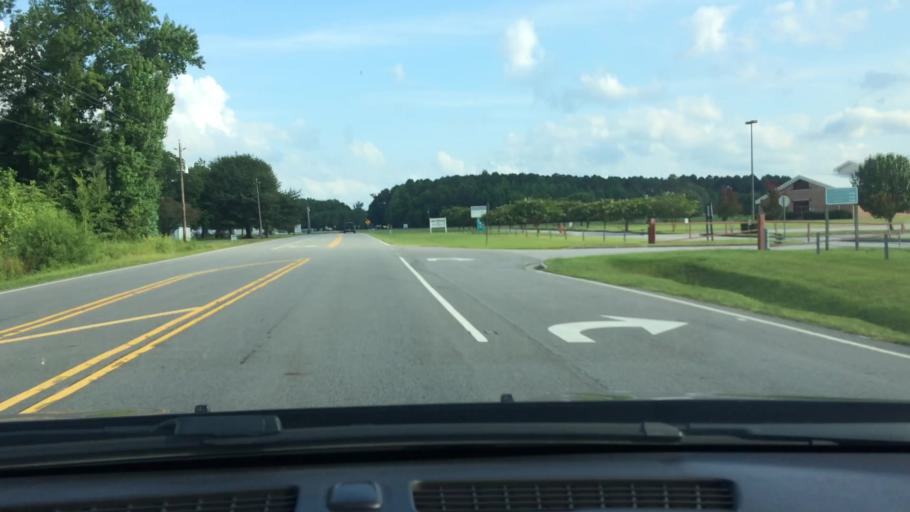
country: US
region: North Carolina
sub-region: Beaufort County
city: River Road
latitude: 35.4473
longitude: -77.0553
